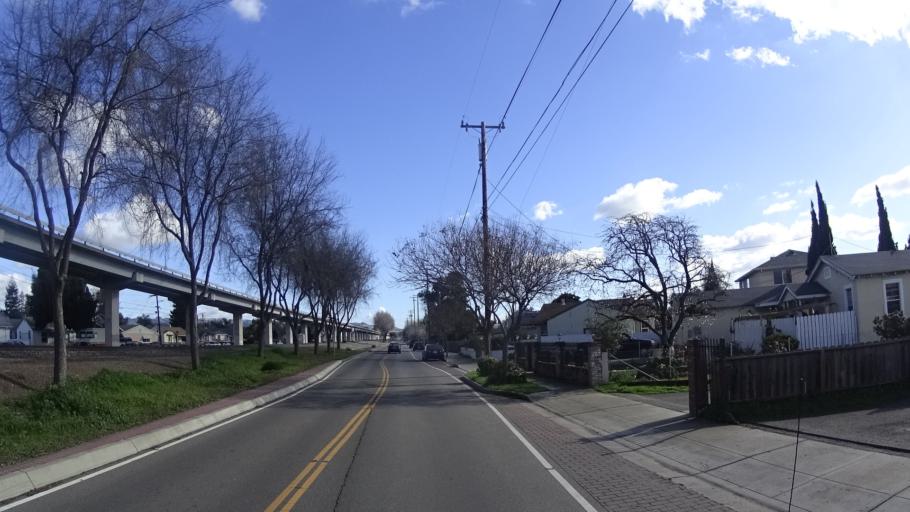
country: US
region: California
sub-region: Alameda County
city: Cherryland
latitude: 37.6814
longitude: -122.1043
